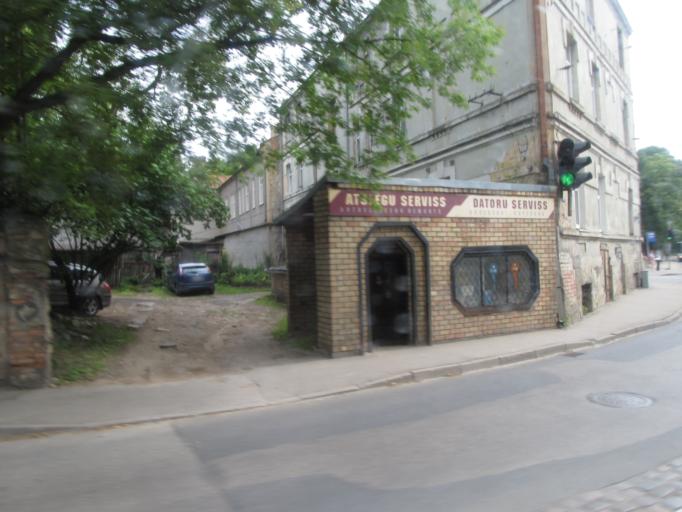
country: LV
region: Riga
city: Riga
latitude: 56.9509
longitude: 24.0645
